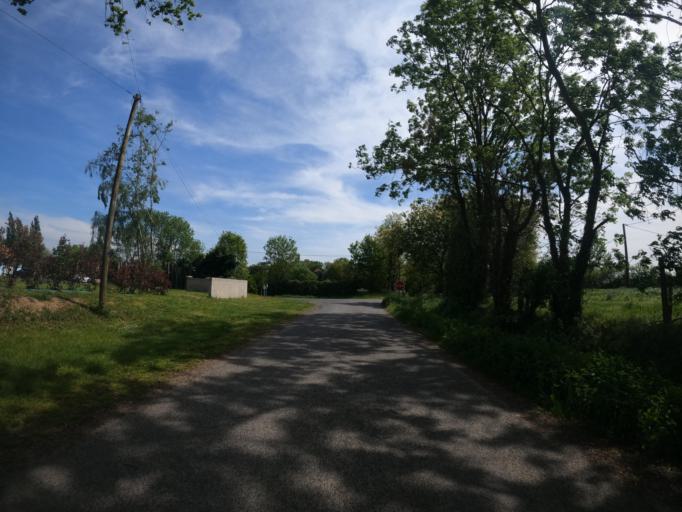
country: FR
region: Poitou-Charentes
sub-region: Departement des Deux-Sevres
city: La Chapelle-Saint-Laurent
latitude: 46.6674
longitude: -0.5066
